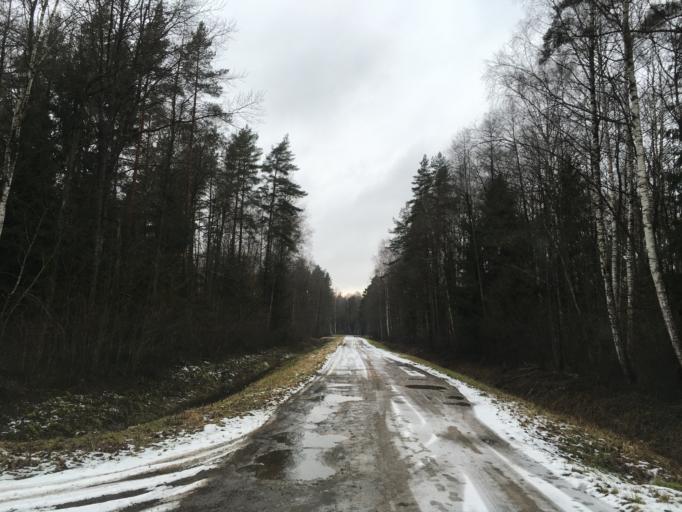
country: LV
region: Ozolnieku
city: Ozolnieki
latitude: 56.6765
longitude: 23.7779
